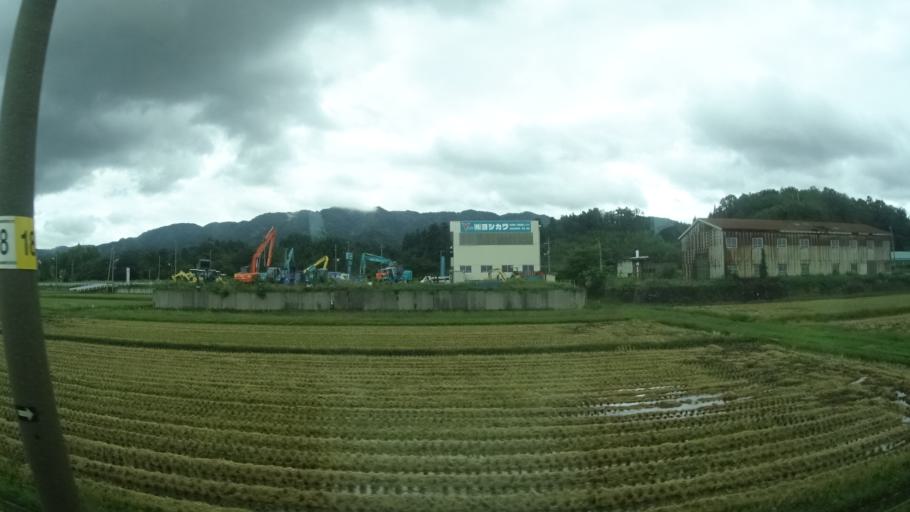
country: JP
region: Niigata
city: Shibata
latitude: 38.0321
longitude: 139.3861
